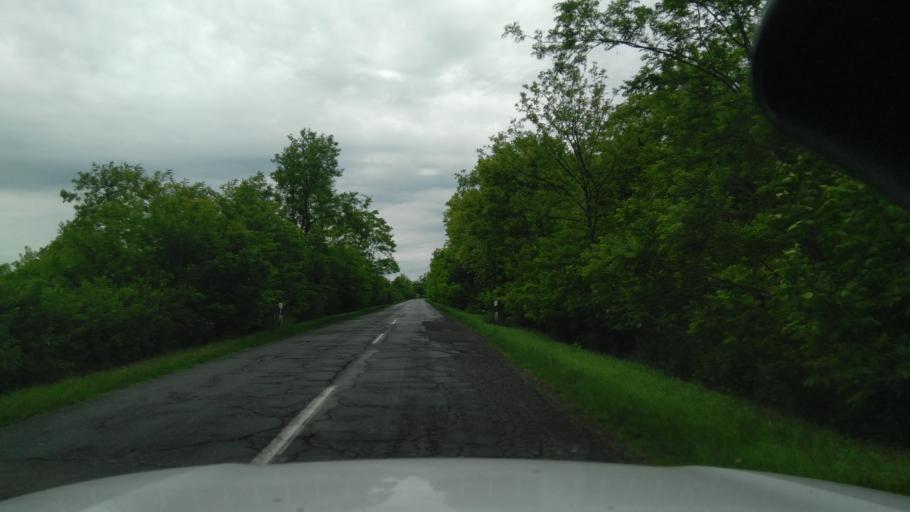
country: HU
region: Bekes
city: Bekescsaba
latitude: 46.6788
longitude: 21.1683
